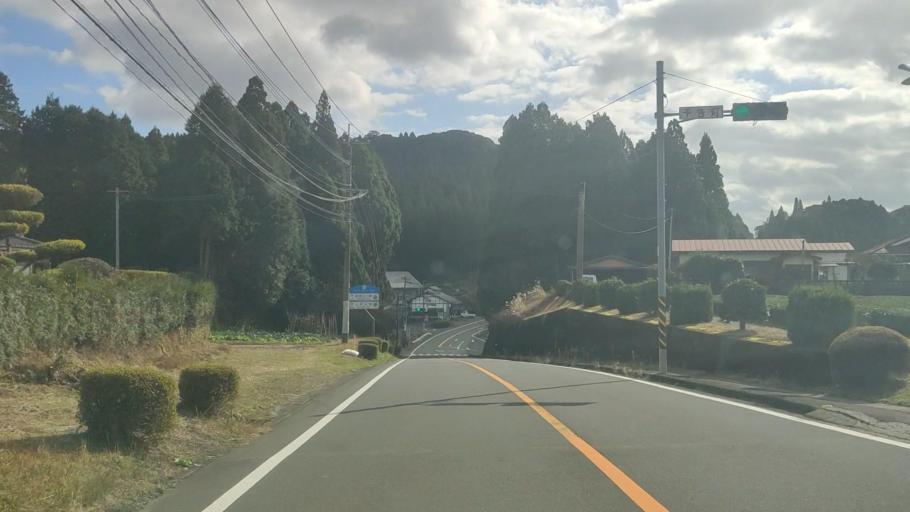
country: JP
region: Kagoshima
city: Kajiki
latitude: 31.8319
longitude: 130.6882
